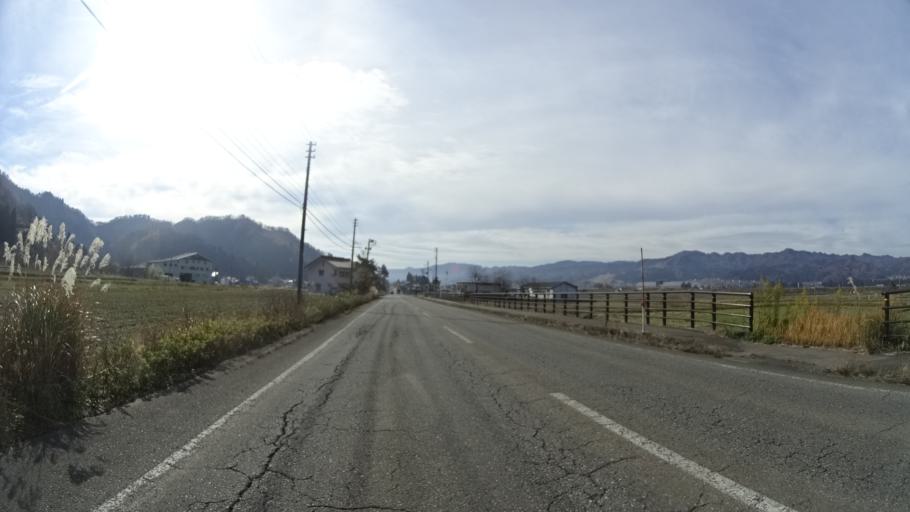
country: JP
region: Niigata
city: Muikamachi
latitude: 37.1269
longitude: 138.9343
